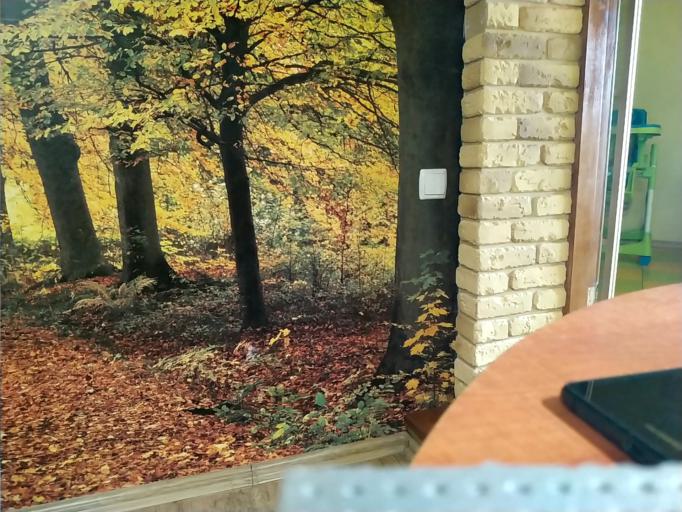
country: RU
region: Tverskaya
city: Kalashnikovo
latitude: 57.2623
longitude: 35.1432
